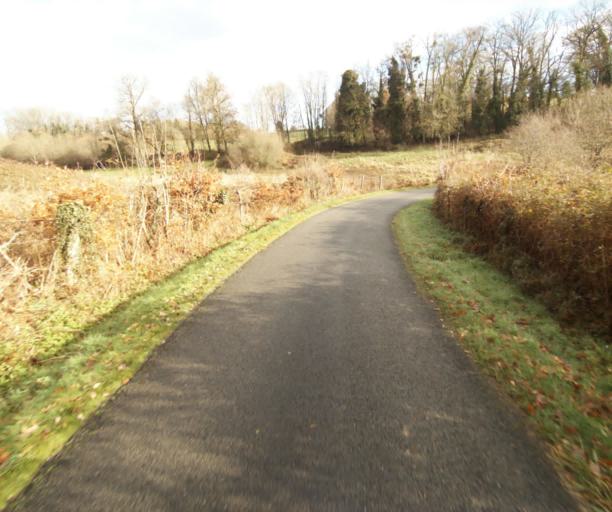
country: FR
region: Limousin
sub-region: Departement de la Correze
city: Sainte-Fereole
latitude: 45.2629
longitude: 1.5981
